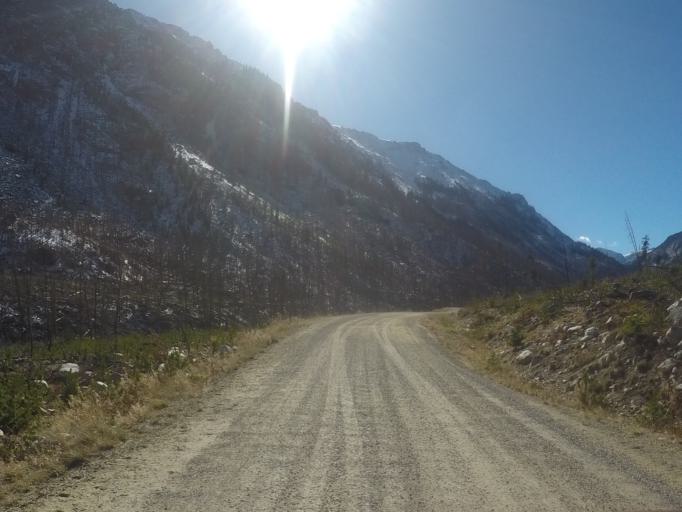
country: US
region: Montana
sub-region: Carbon County
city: Red Lodge
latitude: 45.1692
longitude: -109.4911
